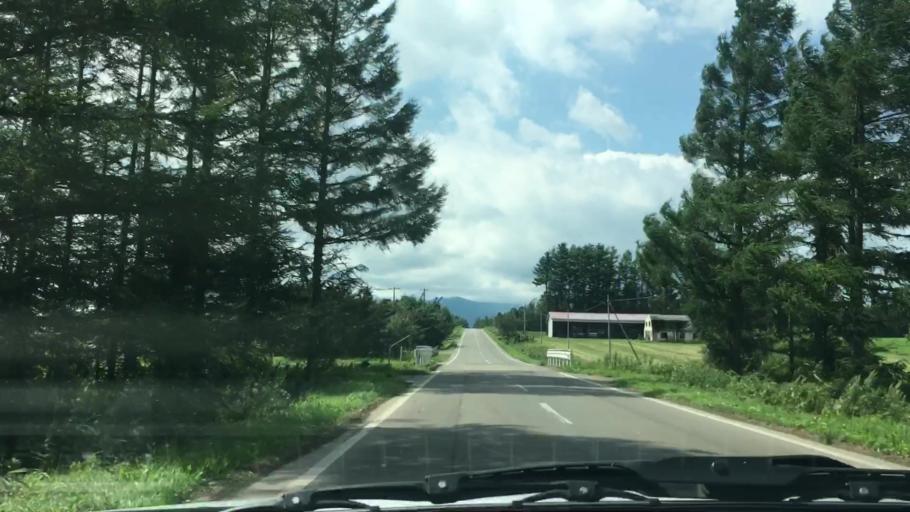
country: JP
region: Hokkaido
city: Otofuke
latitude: 43.2771
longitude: 143.3664
